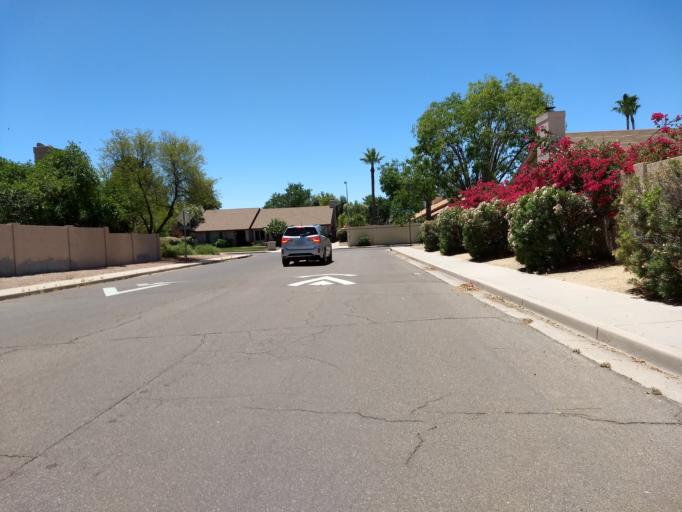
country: US
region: Arizona
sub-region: Maricopa County
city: San Carlos
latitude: 33.3317
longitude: -111.9063
